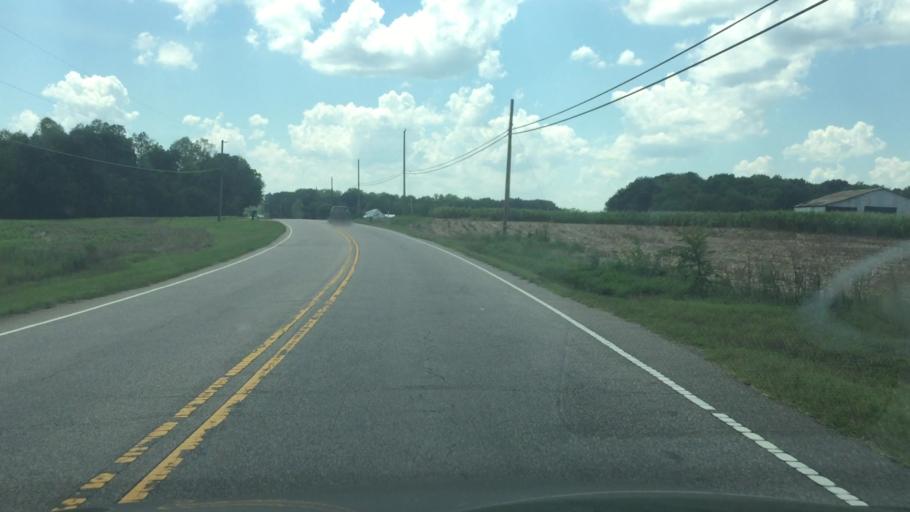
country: US
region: North Carolina
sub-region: Rowan County
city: Enochville
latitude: 35.5777
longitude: -80.6998
